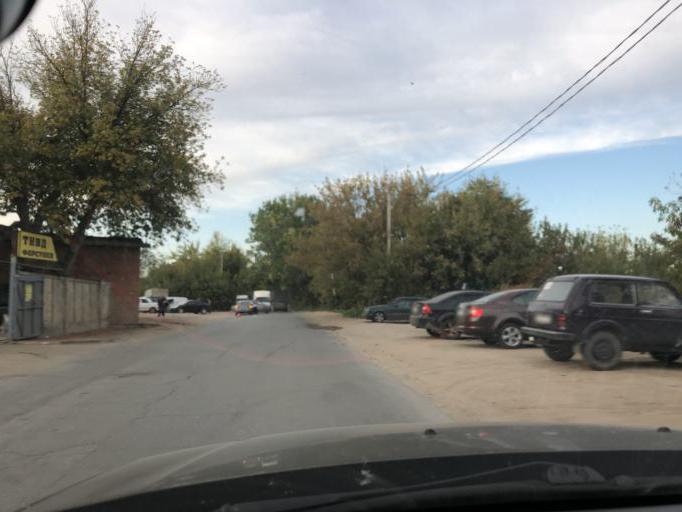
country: RU
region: Tula
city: Tula
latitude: 54.1604
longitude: 37.6169
